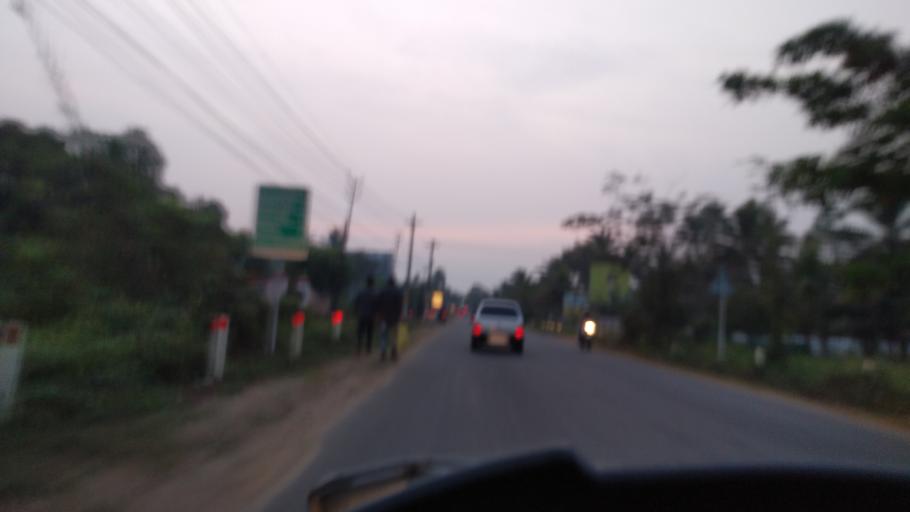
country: IN
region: Kerala
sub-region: Kottayam
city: Kottayam
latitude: 9.5921
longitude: 76.4434
